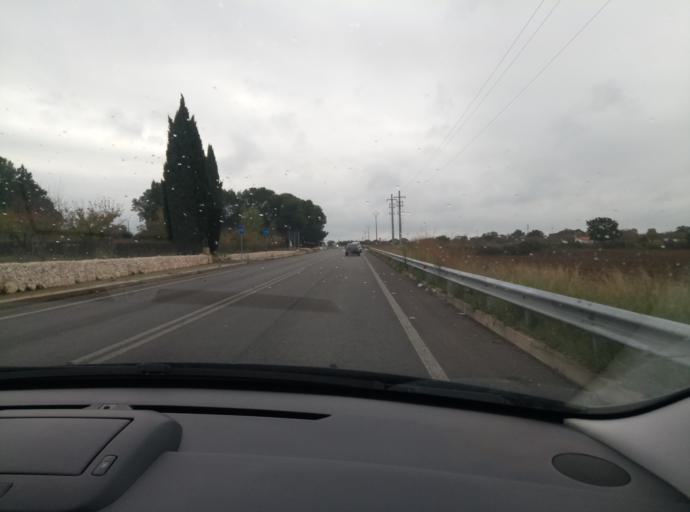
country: IT
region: Apulia
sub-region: Provincia di Bari
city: Acquaviva delle Fonti
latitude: 40.8811
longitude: 16.8115
